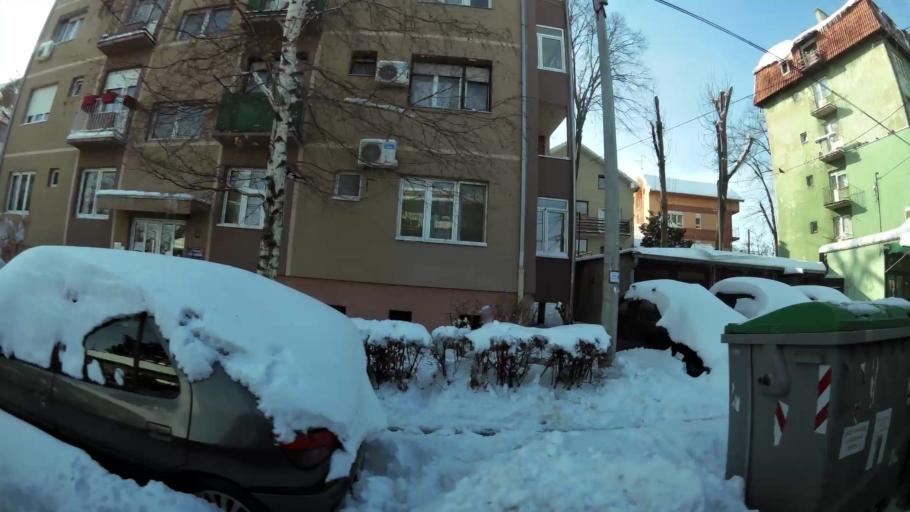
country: RS
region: Central Serbia
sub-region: Belgrade
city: Palilula
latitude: 44.8086
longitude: 20.5180
